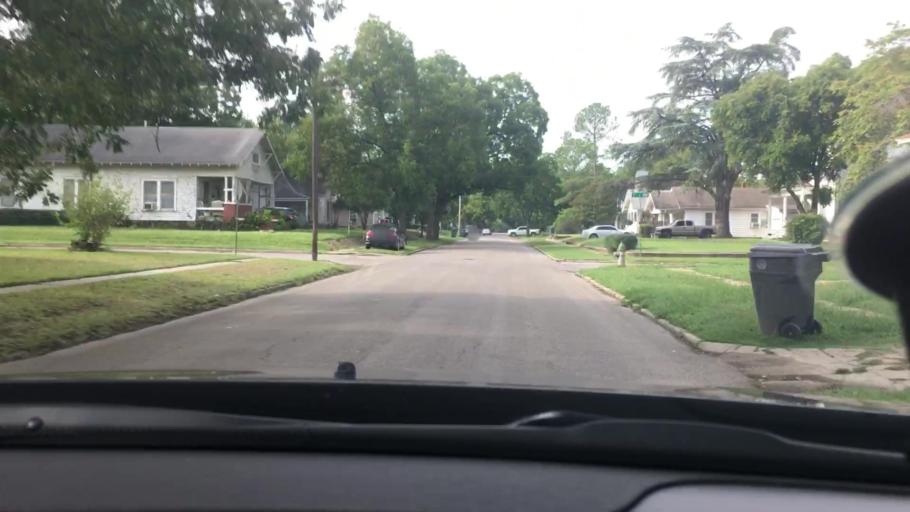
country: US
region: Oklahoma
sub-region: Carter County
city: Ardmore
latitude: 34.1809
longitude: -97.1285
